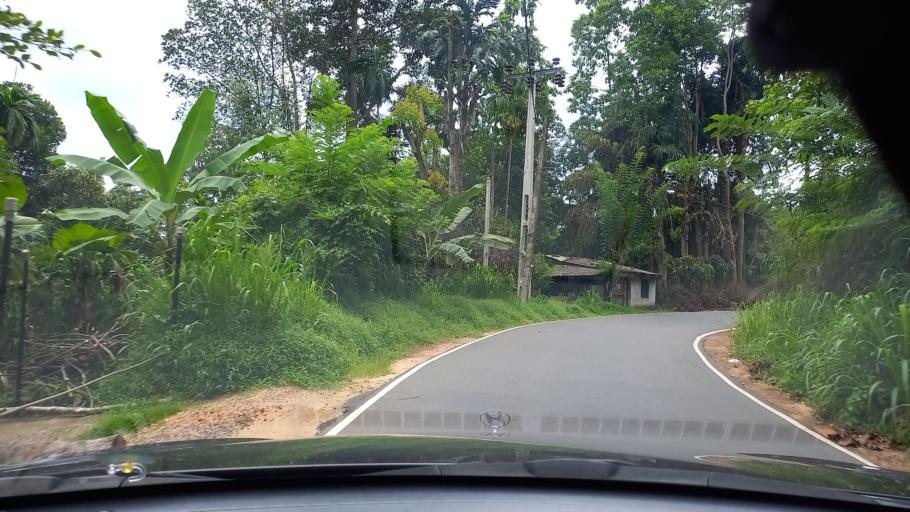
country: LK
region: Central
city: Gampola
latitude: 7.2208
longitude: 80.6090
